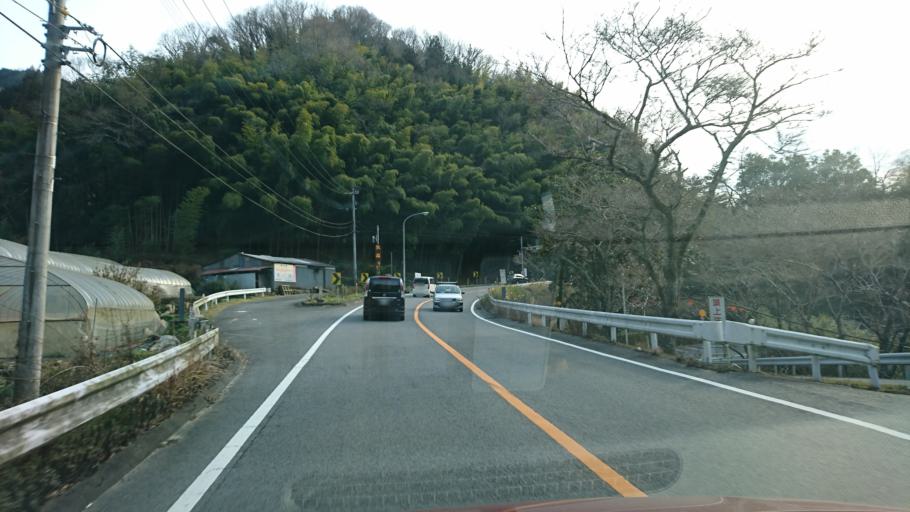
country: JP
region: Ehime
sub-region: Shikoku-chuo Shi
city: Matsuyama
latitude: 33.8952
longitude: 132.8438
